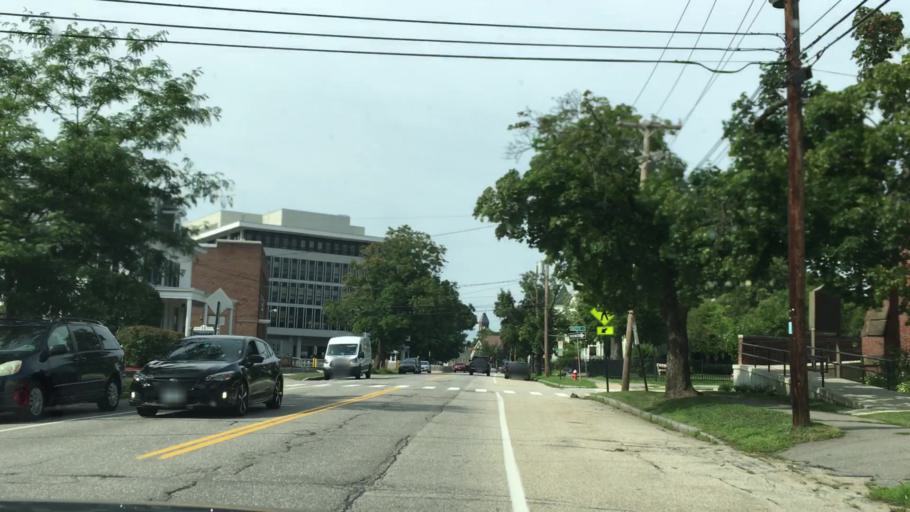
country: US
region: New Hampshire
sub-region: Merrimack County
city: Concord
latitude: 43.2006
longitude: -71.5389
